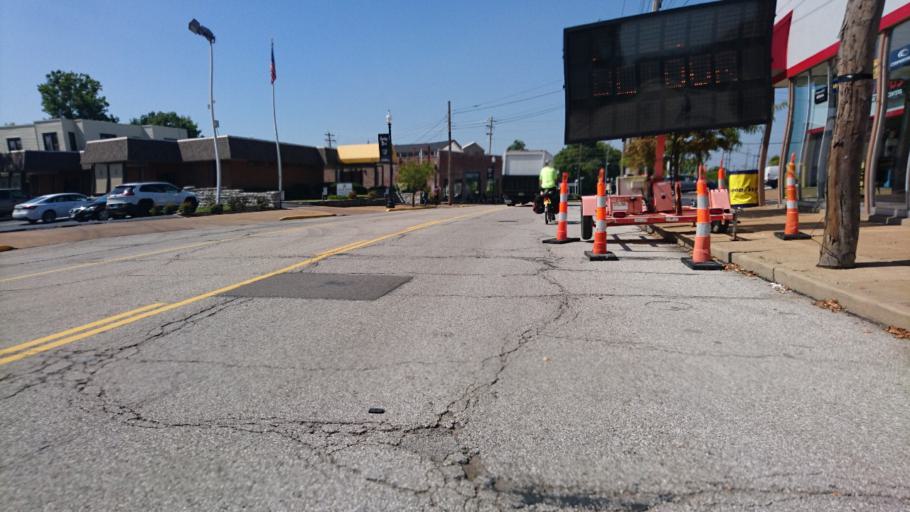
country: US
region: Missouri
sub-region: Saint Louis County
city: Maplewood
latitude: 38.6124
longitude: -90.3210
